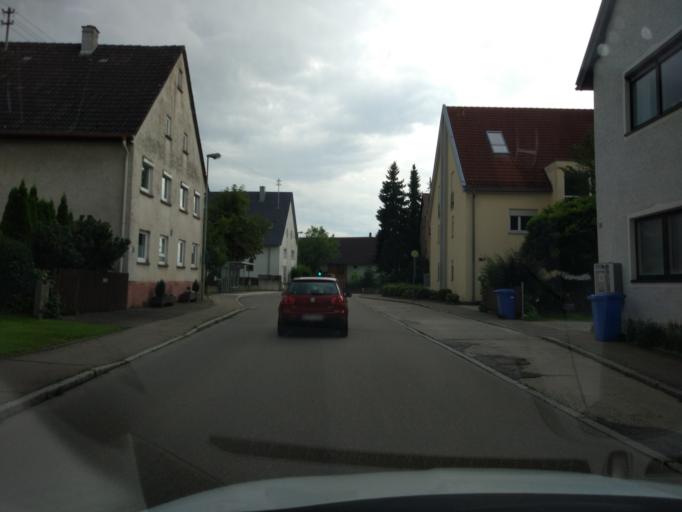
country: DE
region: Baden-Wuerttemberg
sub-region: Tuebingen Region
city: Erbach
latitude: 48.3390
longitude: 9.9393
